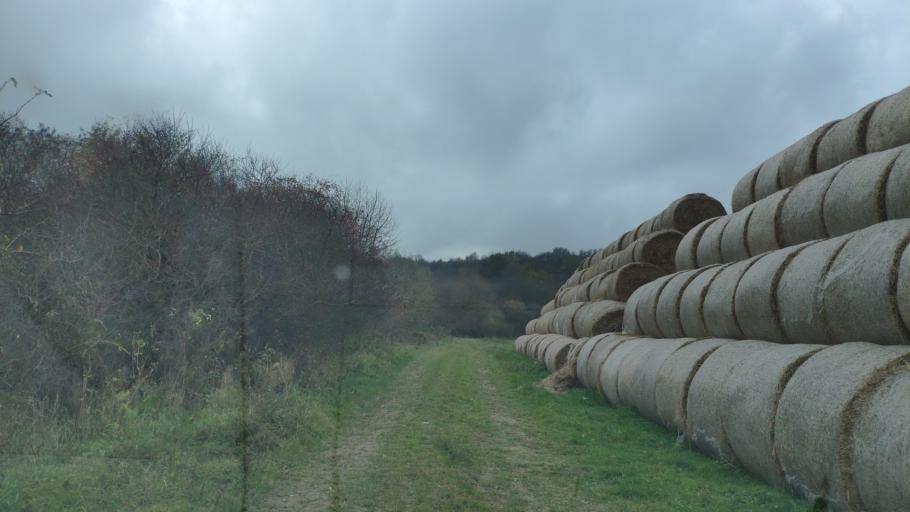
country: SK
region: Presovsky
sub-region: Okres Presov
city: Presov
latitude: 49.0138
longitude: 21.2004
